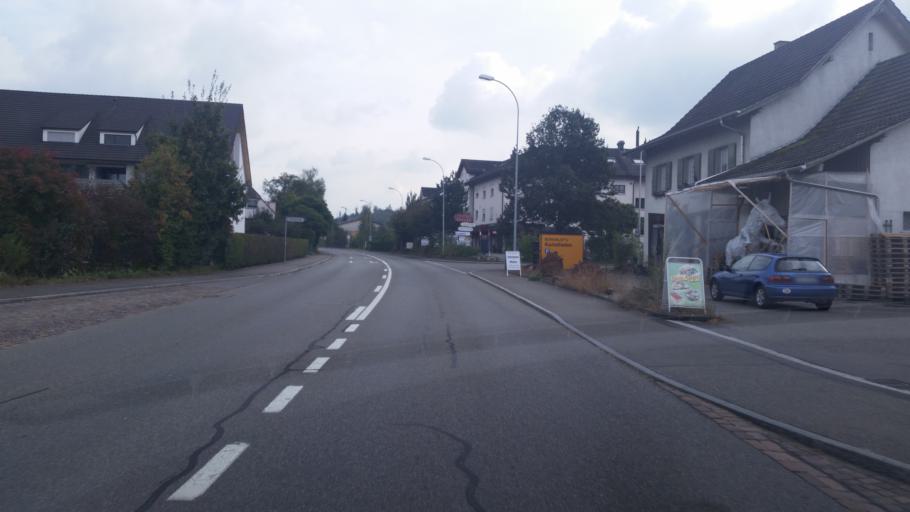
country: CH
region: Aargau
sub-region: Bezirk Baden
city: Kunten
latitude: 47.3709
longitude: 8.3082
